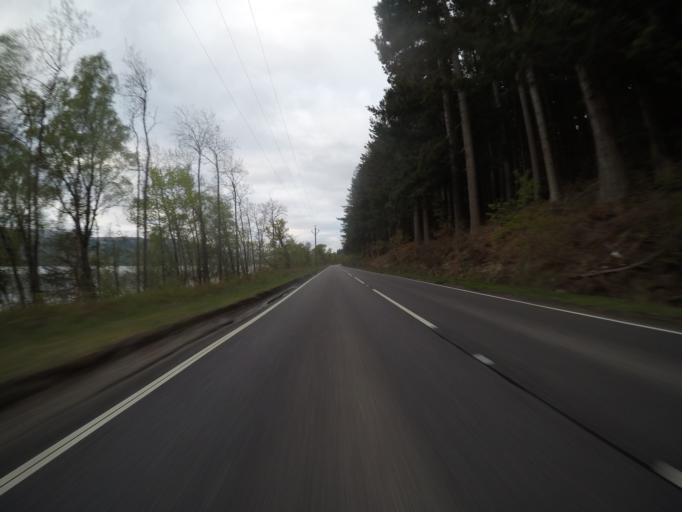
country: GB
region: Scotland
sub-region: Highland
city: Beauly
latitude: 57.1687
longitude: -4.6471
